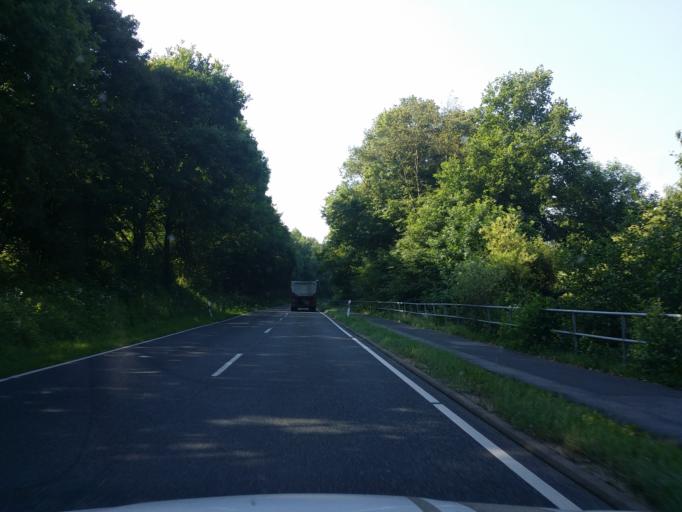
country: DE
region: Hesse
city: Eppstein
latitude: 50.1645
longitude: 8.3766
